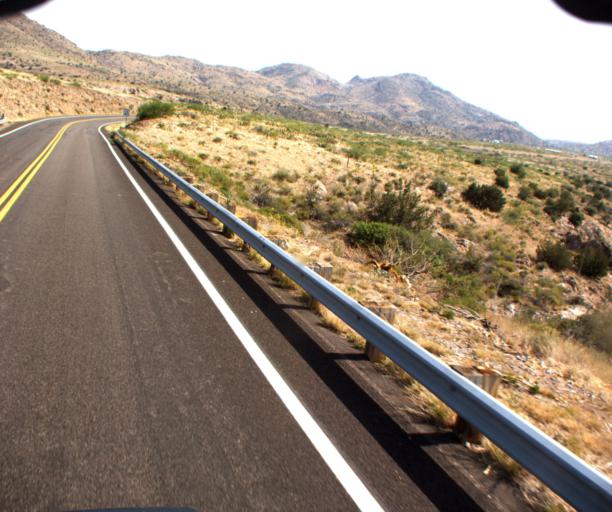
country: US
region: Arizona
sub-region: Greenlee County
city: Clifton
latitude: 33.0472
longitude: -109.1129
